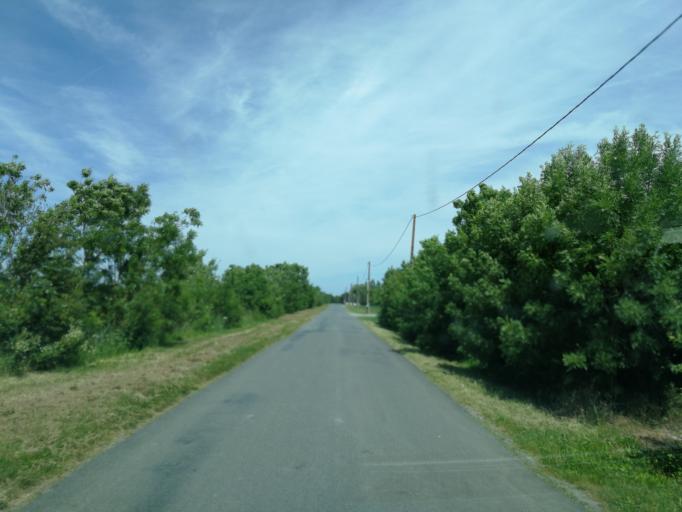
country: FR
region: Pays de la Loire
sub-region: Departement de la Vendee
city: Le Langon
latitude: 46.3910
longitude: -0.9373
